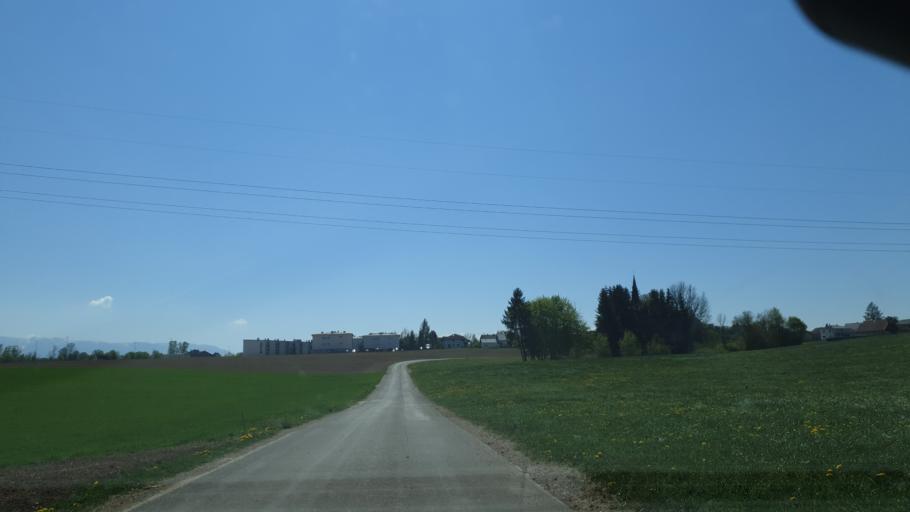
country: AT
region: Upper Austria
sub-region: Politischer Bezirk Vocklabruck
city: Gampern
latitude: 47.9936
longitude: 13.5589
